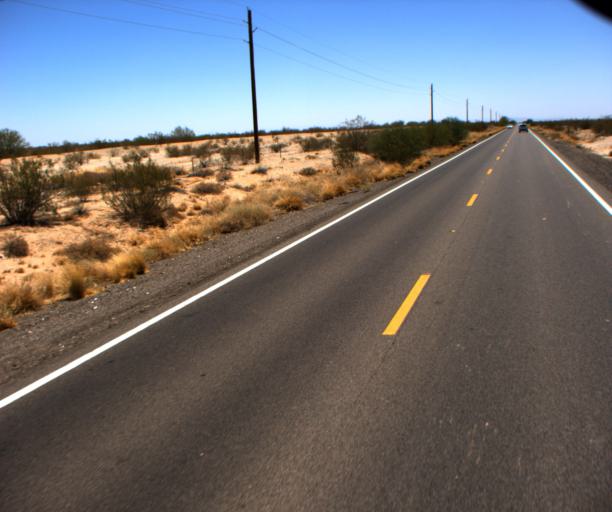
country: US
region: Arizona
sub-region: Pinal County
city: Maricopa
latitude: 33.0745
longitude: -112.1767
